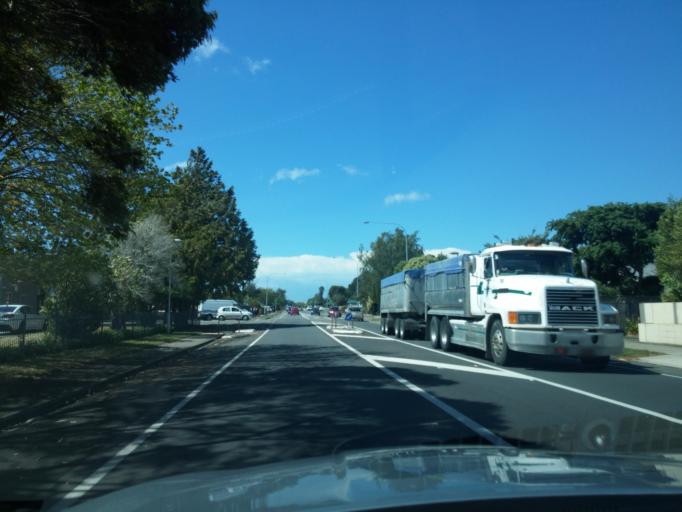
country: NZ
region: Marlborough
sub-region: Marlborough District
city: Blenheim
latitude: -41.5087
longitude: 173.9443
